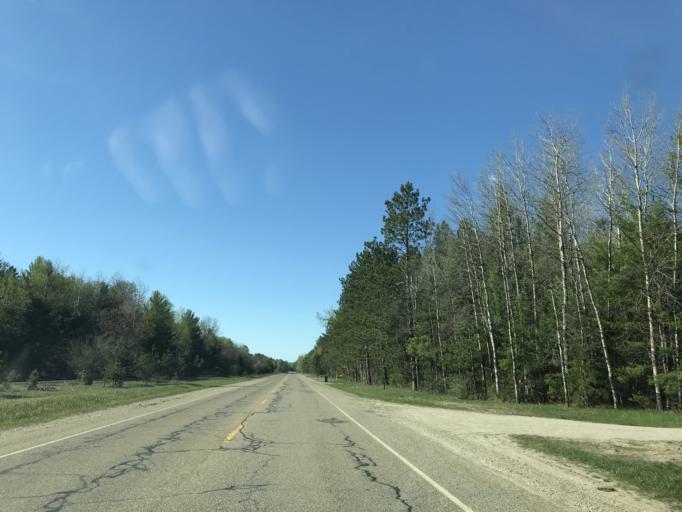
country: US
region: Michigan
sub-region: Crawford County
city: Grayling
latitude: 44.7522
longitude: -84.7523
